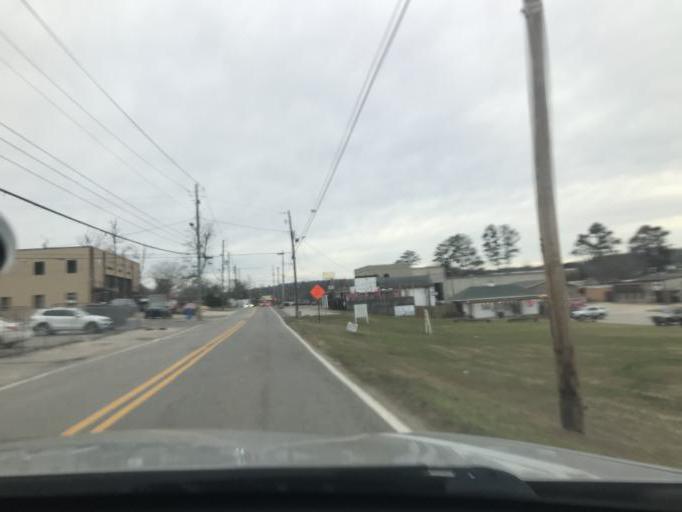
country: US
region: Alabama
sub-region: Jefferson County
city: Cahaba Heights
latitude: 33.4541
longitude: -86.7277
